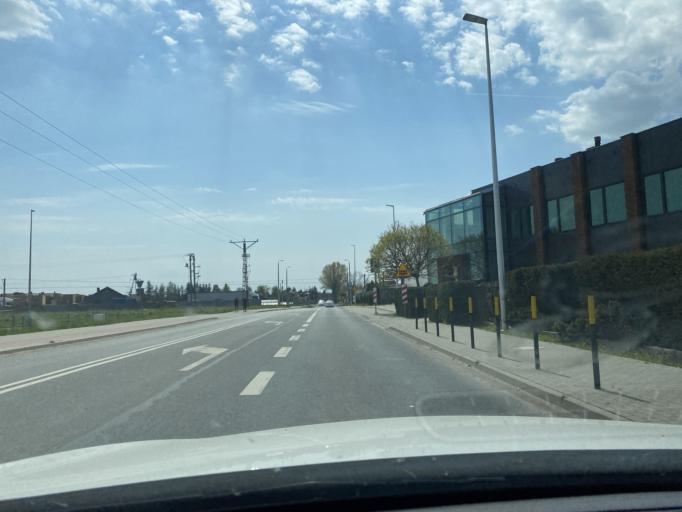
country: PL
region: Lower Silesian Voivodeship
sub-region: Powiat wroclawski
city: Mirkow
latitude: 51.1661
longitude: 17.1641
